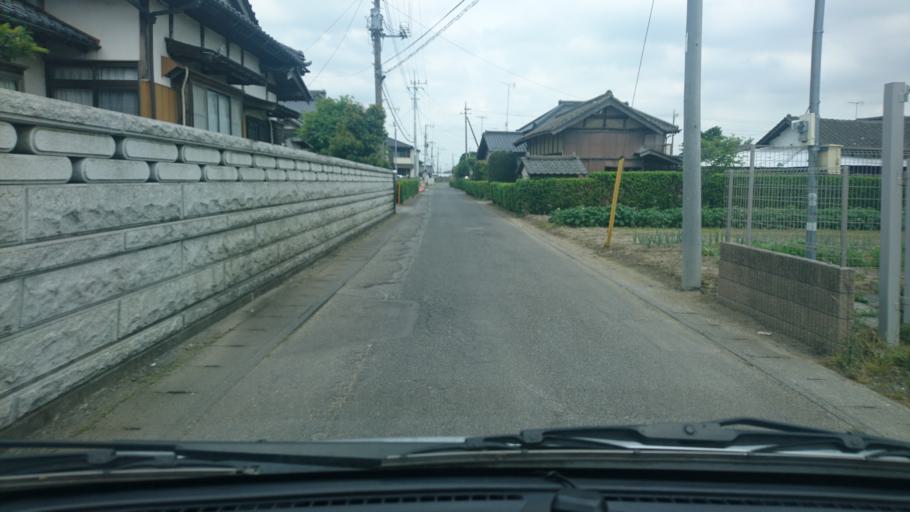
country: JP
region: Ibaraki
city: Ishige
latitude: 36.1028
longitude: 139.9763
